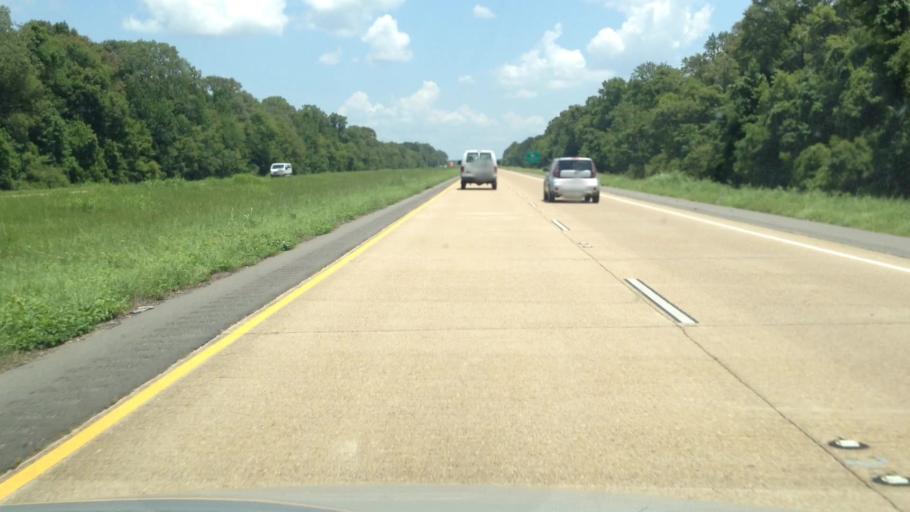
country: US
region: Louisiana
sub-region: Rapides Parish
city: Lecompte
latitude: 30.9973
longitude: -92.3325
